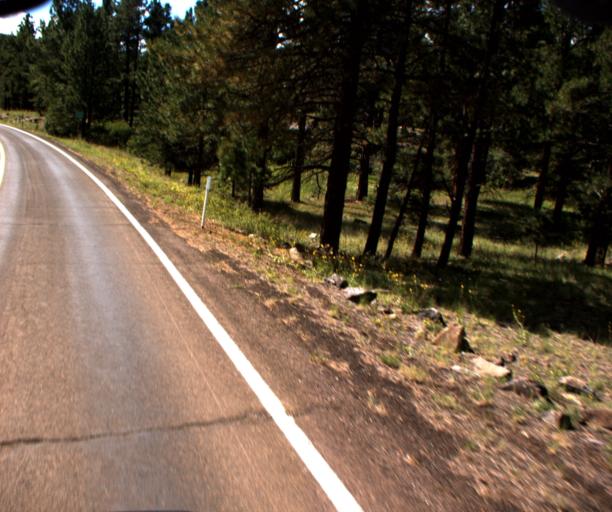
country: US
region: Arizona
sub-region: Apache County
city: Eagar
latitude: 34.0418
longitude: -109.4589
